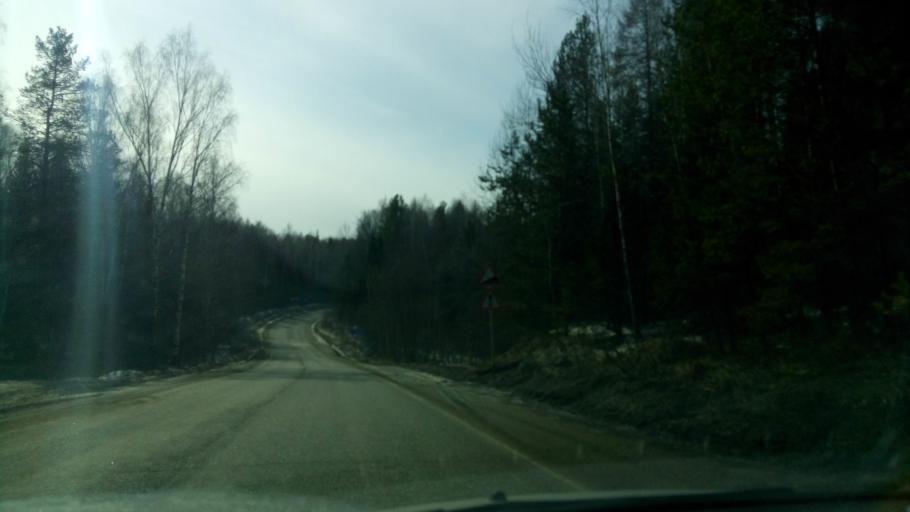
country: RU
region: Sverdlovsk
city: Chernoistochinsk
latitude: 57.6992
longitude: 59.7620
